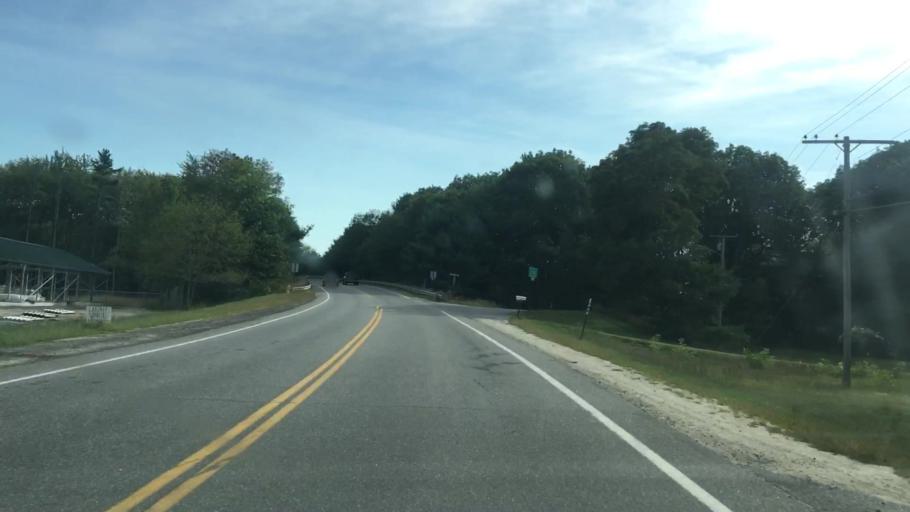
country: US
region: Maine
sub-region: Cumberland County
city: Brunswick
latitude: 43.9145
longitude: -69.9066
